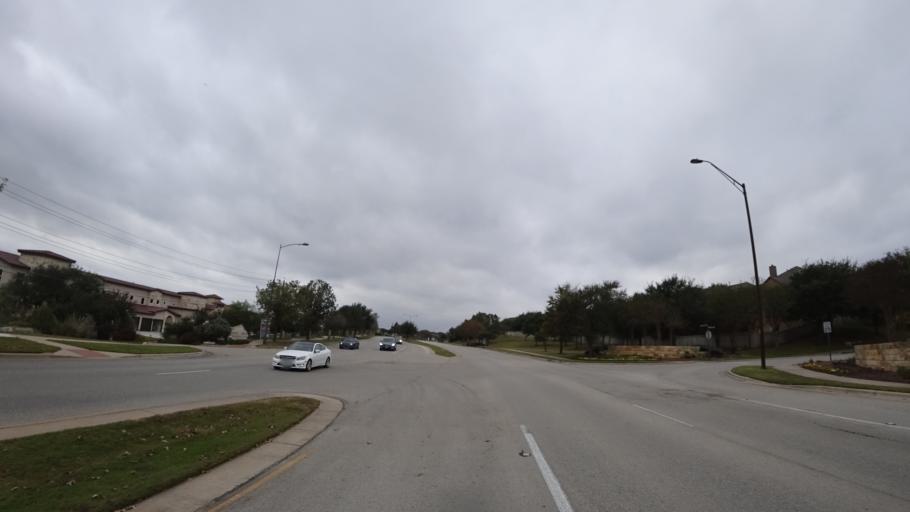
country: US
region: Texas
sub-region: Travis County
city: Hudson Bend
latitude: 30.3664
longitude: -97.8959
